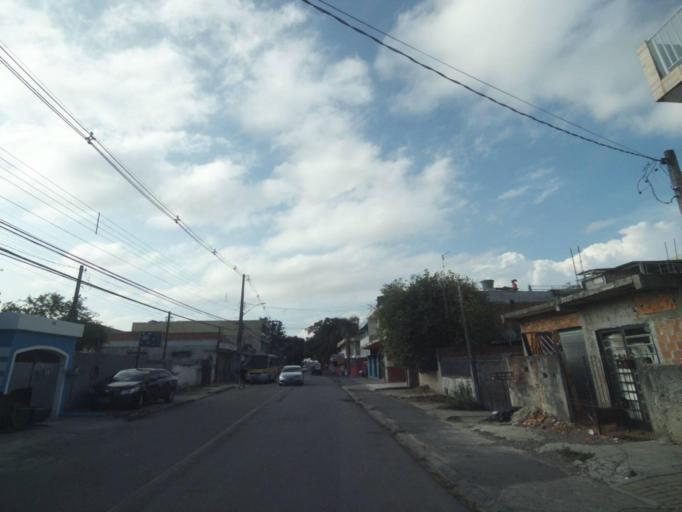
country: BR
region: Parana
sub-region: Araucaria
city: Araucaria
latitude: -25.5326
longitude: -49.3345
